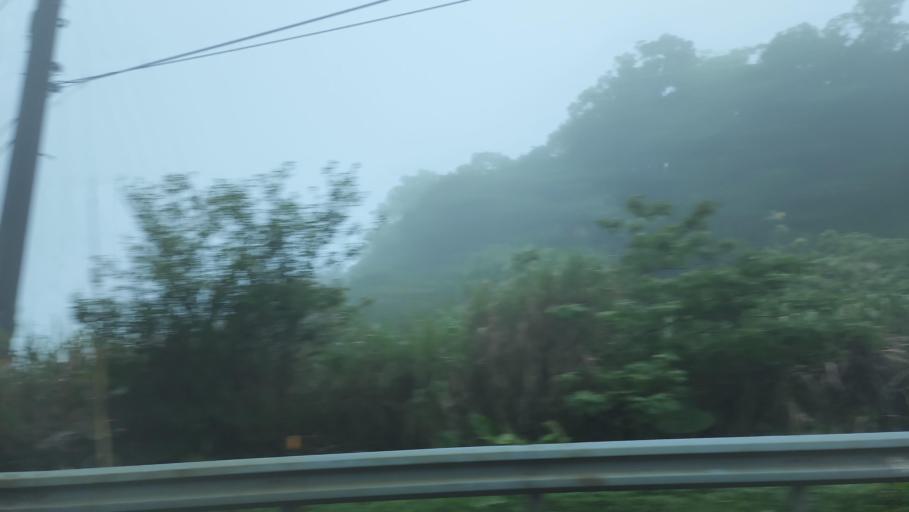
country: TW
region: Taipei
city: Taipei
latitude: 25.1382
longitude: 121.6031
